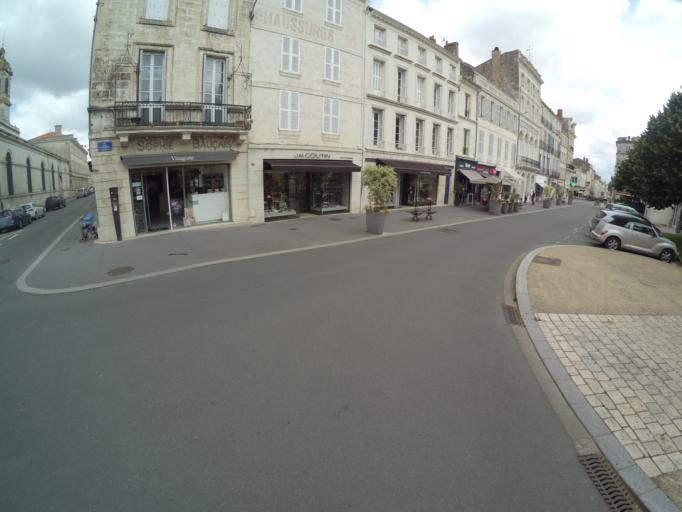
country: FR
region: Poitou-Charentes
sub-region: Departement de la Charente-Maritime
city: Rochefort
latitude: 45.9372
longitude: -0.9620
